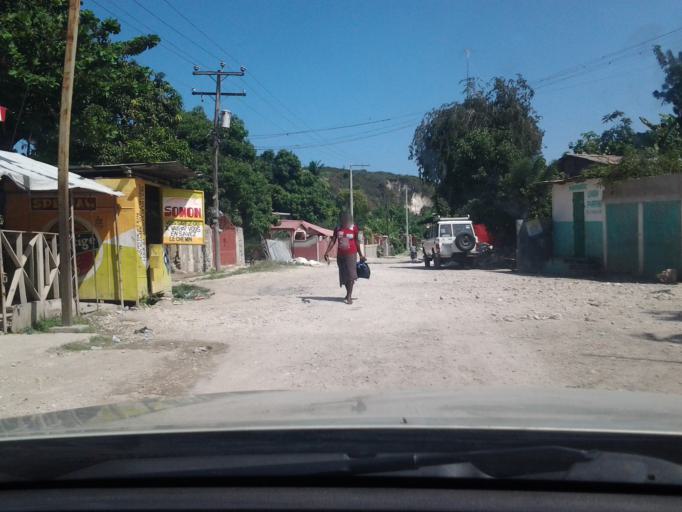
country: HT
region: Ouest
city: Tigwav
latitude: 18.4400
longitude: -72.8484
